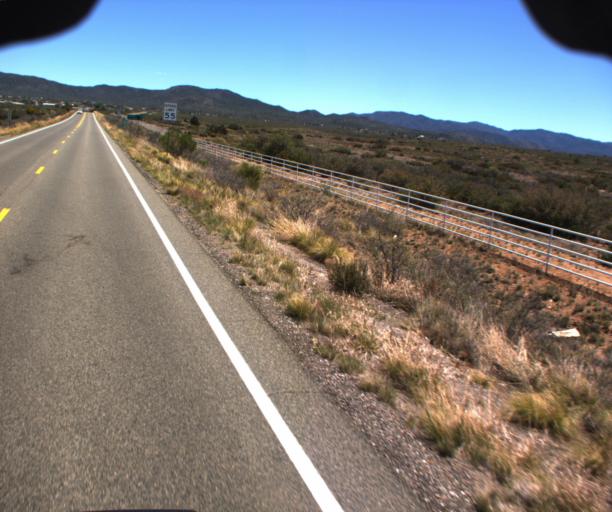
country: US
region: Arizona
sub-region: Yavapai County
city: Prescott
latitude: 34.4071
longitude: -112.6167
